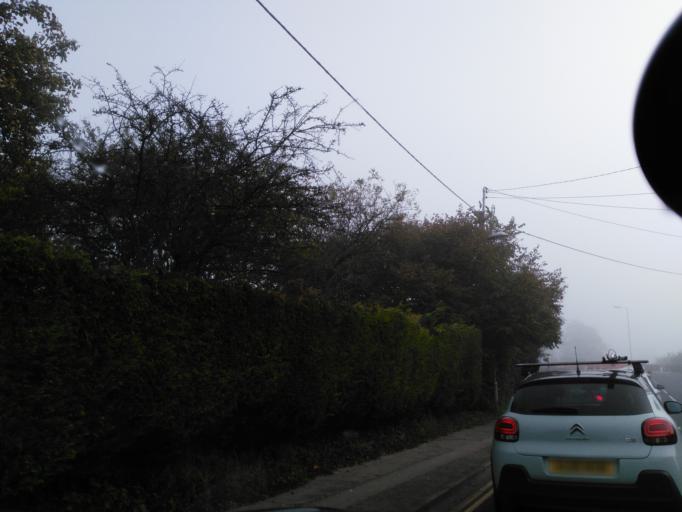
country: GB
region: England
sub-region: Wiltshire
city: Devizes
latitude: 51.3524
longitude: -2.0118
